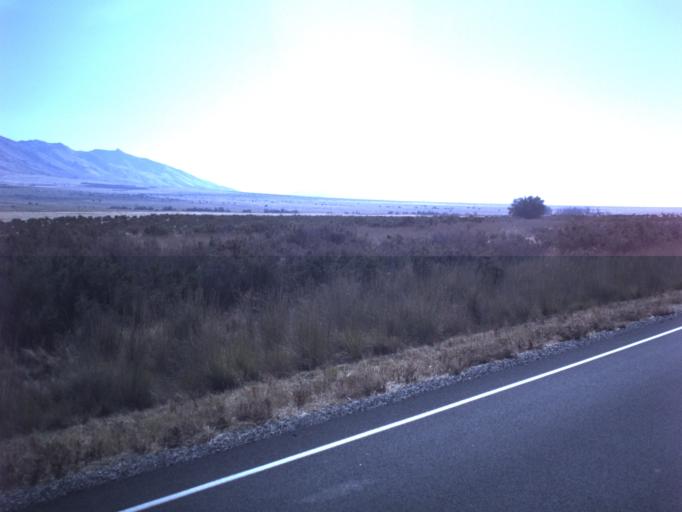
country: US
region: Utah
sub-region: Tooele County
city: Grantsville
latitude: 40.4735
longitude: -112.7462
